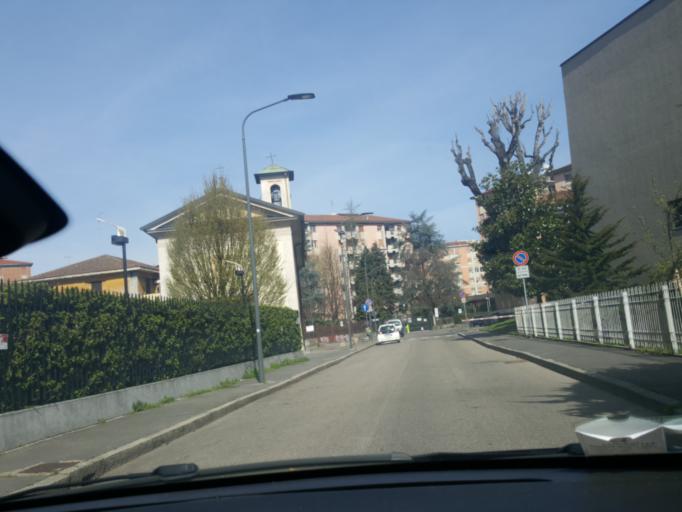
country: IT
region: Lombardy
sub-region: Citta metropolitana di Milano
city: Novate Milanese
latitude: 45.4942
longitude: 9.1345
